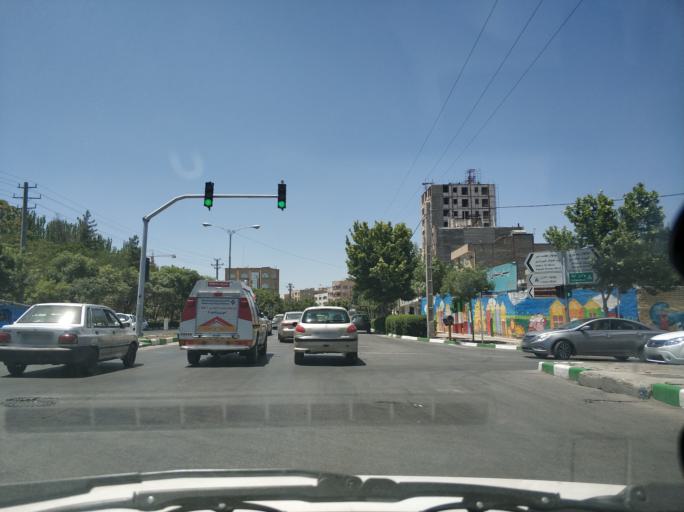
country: IR
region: Razavi Khorasan
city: Mashhad
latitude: 36.3108
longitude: 59.4973
